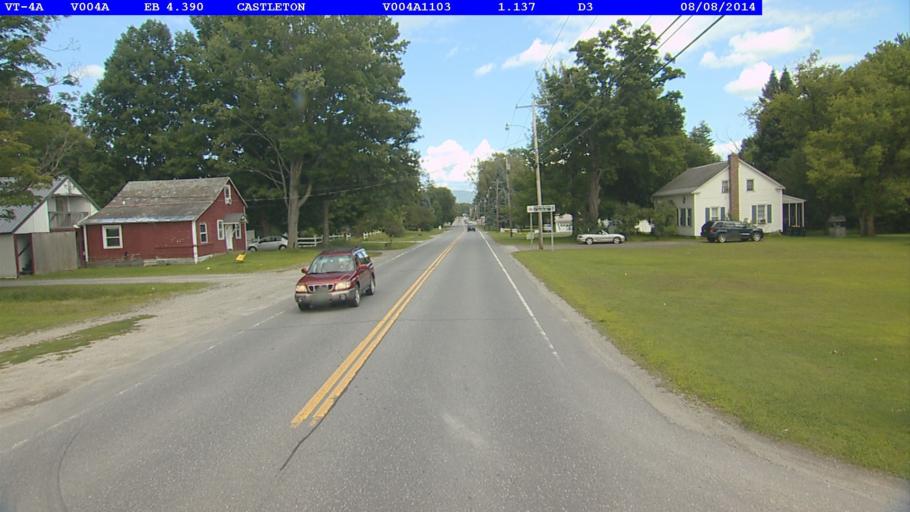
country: US
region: Vermont
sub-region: Rutland County
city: Castleton
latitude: 43.6077
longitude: -73.2212
